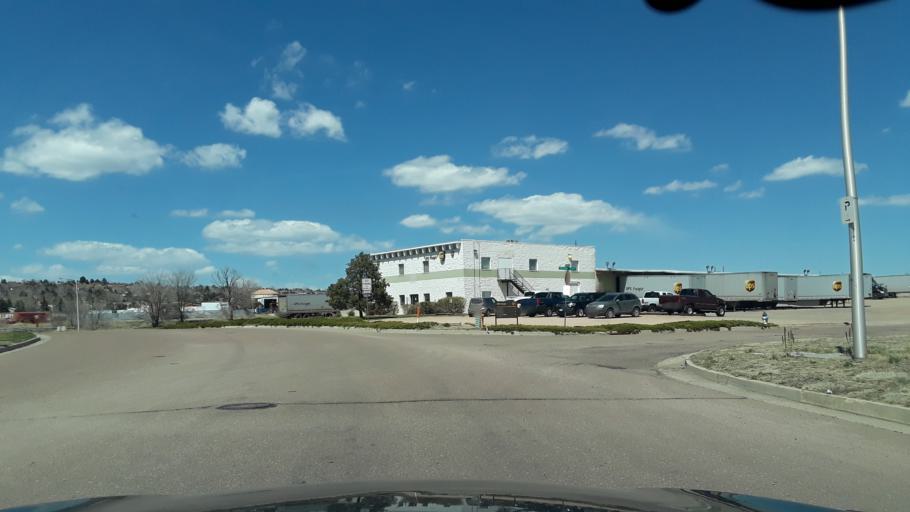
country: US
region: Colorado
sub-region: El Paso County
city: Cimarron Hills
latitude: 38.8662
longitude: -104.7153
